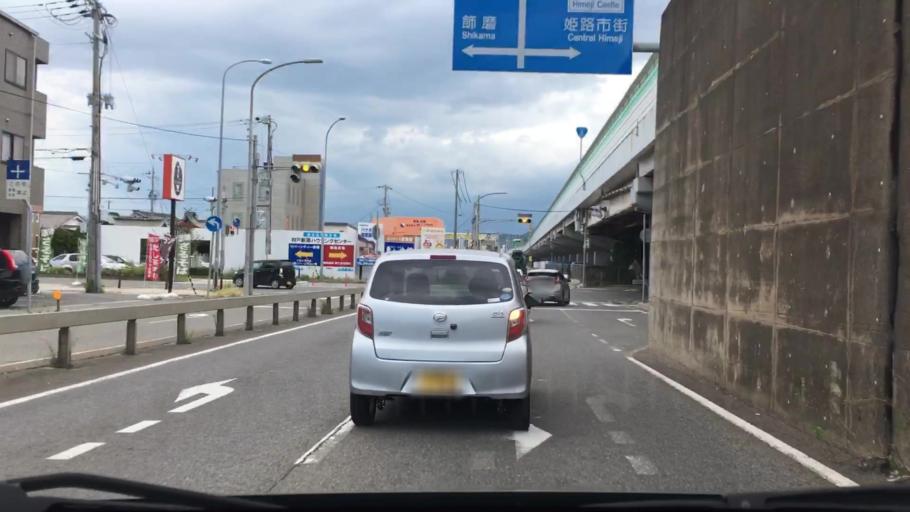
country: JP
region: Hyogo
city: Himeji
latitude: 34.8087
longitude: 134.6915
